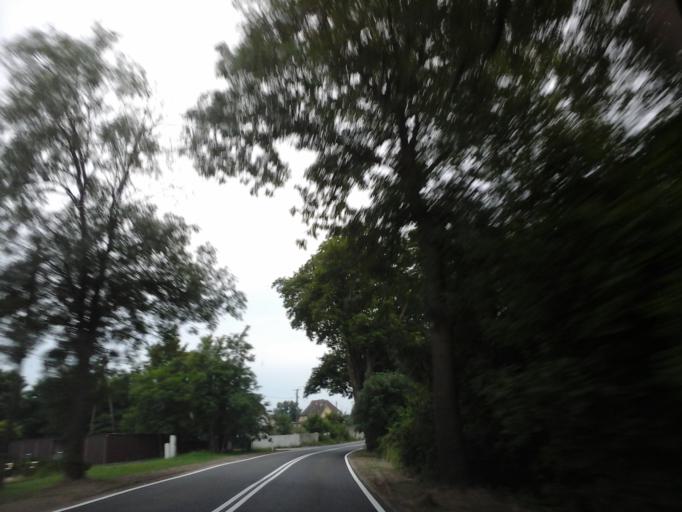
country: PL
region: West Pomeranian Voivodeship
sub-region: Powiat goleniowski
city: Maszewo
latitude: 53.4854
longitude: 15.0631
